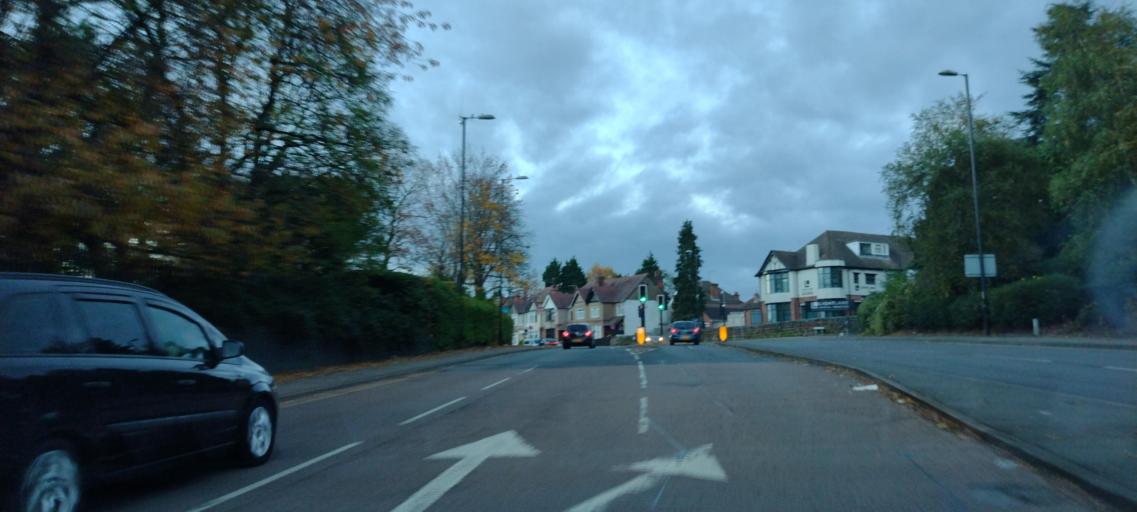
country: GB
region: England
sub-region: Coventry
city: Coventry
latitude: 52.4141
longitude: -1.5149
